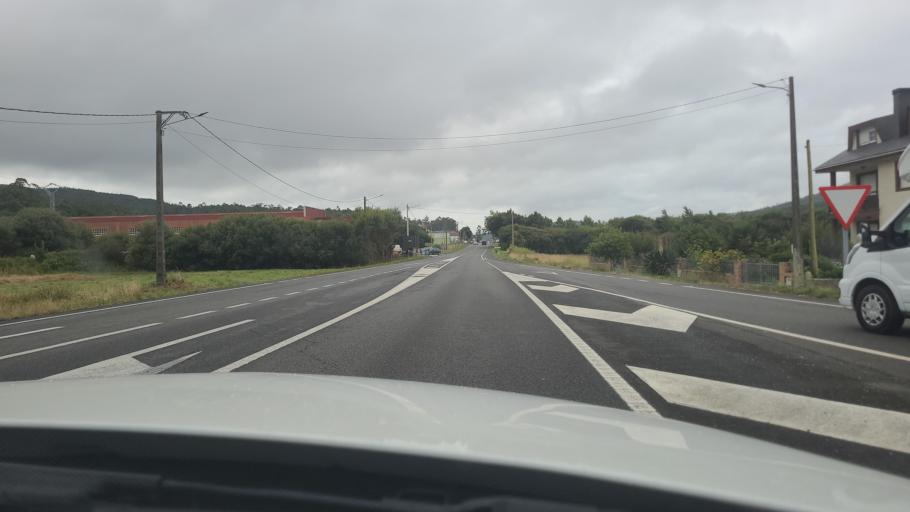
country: ES
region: Galicia
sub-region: Provincia da Coruna
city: Cee
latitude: 42.9864
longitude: -9.1851
